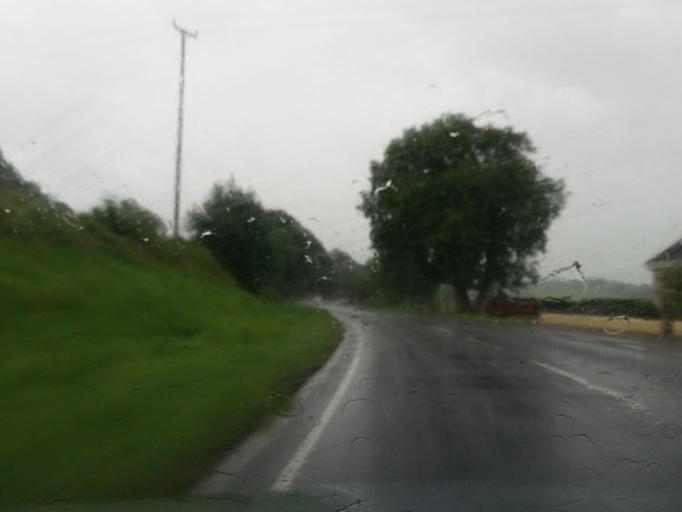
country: GB
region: Northern Ireland
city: Lisnaskea
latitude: 54.2214
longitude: -7.4113
